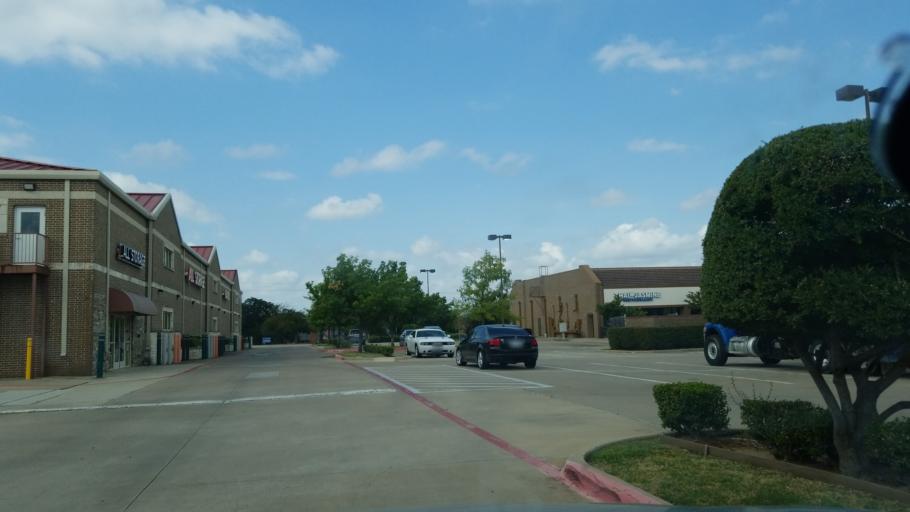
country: US
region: Texas
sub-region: Tarrant County
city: Bedford
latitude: 32.8511
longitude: -97.1157
